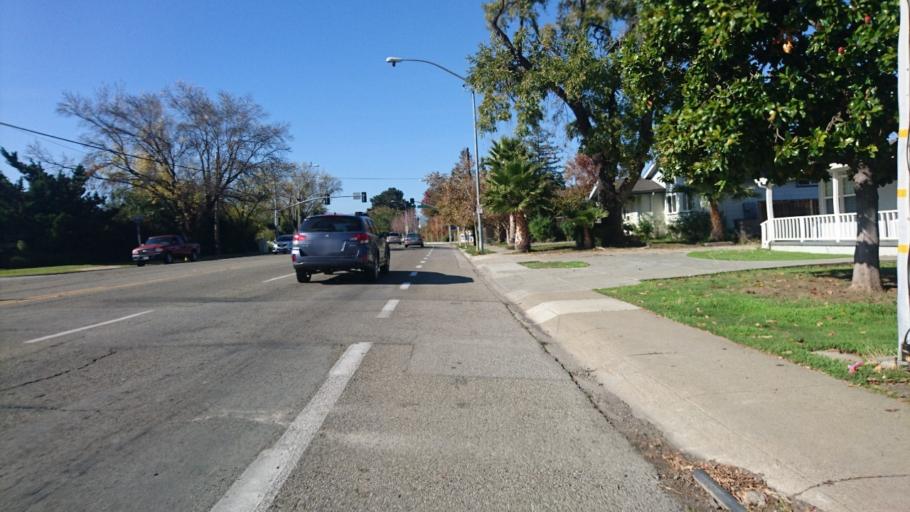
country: US
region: California
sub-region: Santa Clara County
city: Campbell
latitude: 37.2869
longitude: -121.9659
